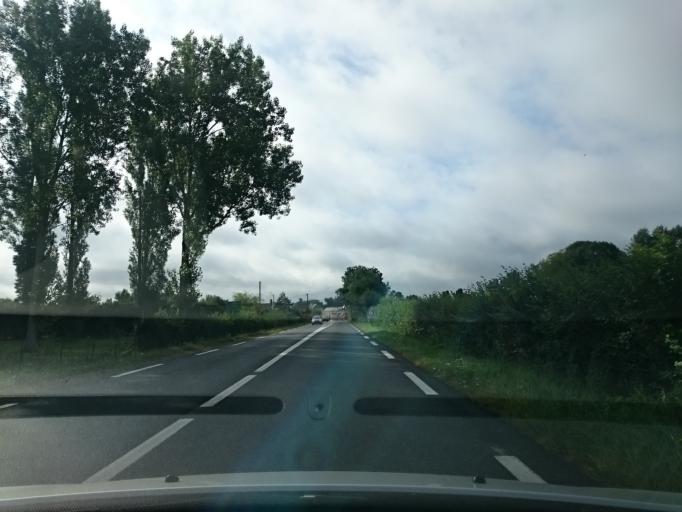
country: FR
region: Lower Normandy
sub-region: Departement du Calvados
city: Cambremer
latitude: 49.1211
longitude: 0.0123
